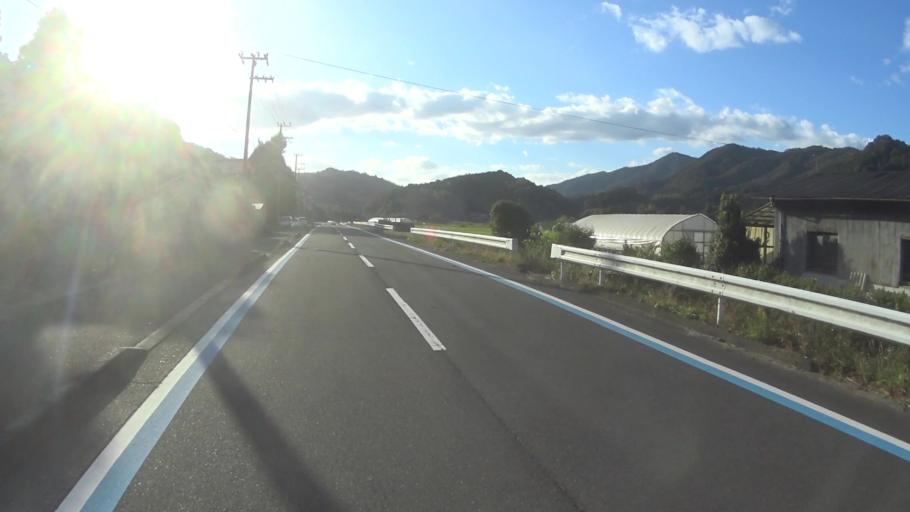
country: JP
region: Kyoto
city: Miyazu
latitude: 35.4182
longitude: 135.2097
